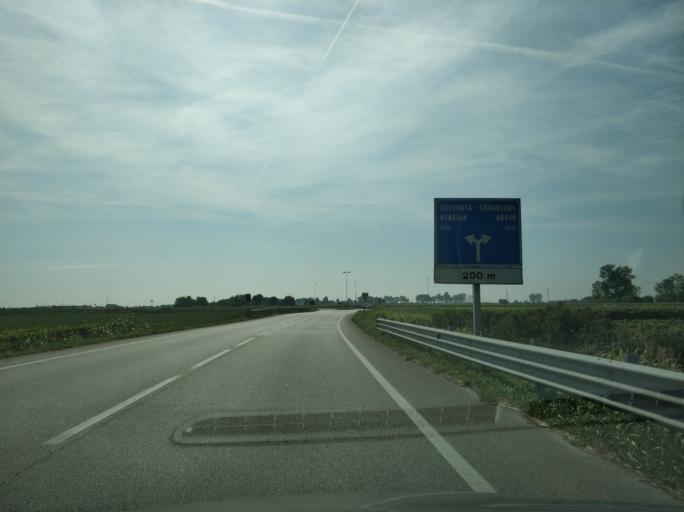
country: IT
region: Veneto
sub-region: Provincia di Padova
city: Correzzola
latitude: 45.2166
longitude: 12.1025
